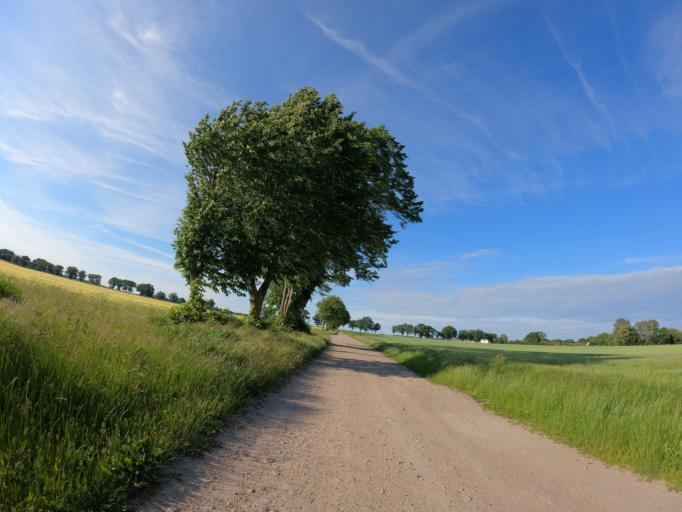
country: DE
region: Mecklenburg-Vorpommern
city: Preetz
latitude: 54.3453
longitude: 13.0002
